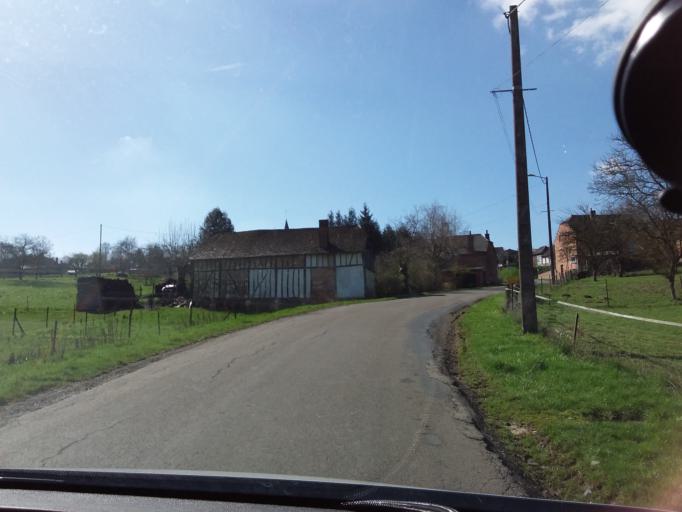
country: FR
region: Picardie
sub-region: Departement de l'Aisne
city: Montcornet
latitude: 49.7792
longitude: 4.0049
